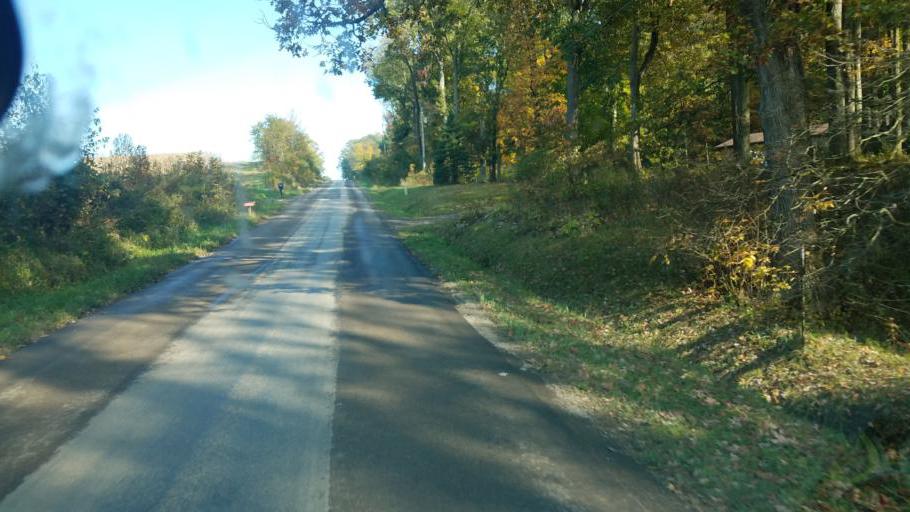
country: US
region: Ohio
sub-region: Wayne County
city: Apple Creek
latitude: 40.6746
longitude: -81.8575
